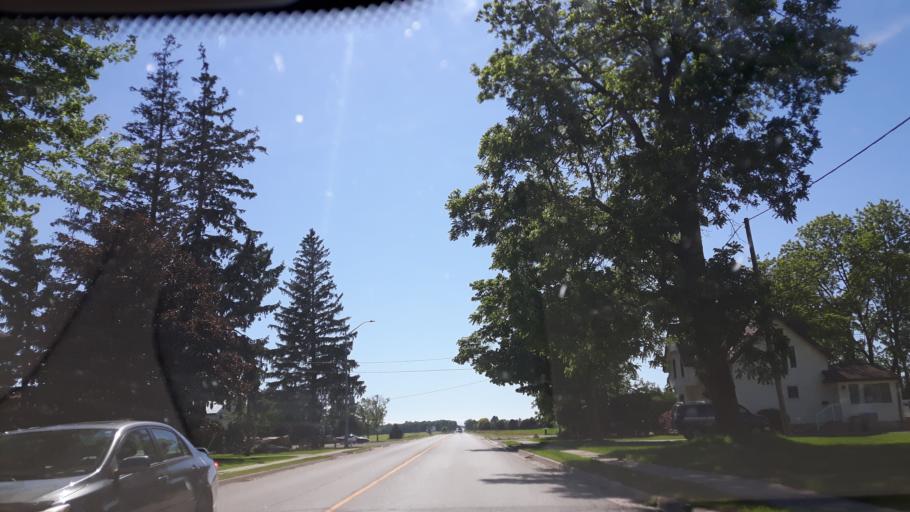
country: CA
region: Ontario
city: Bluewater
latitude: 43.4334
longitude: -81.5098
